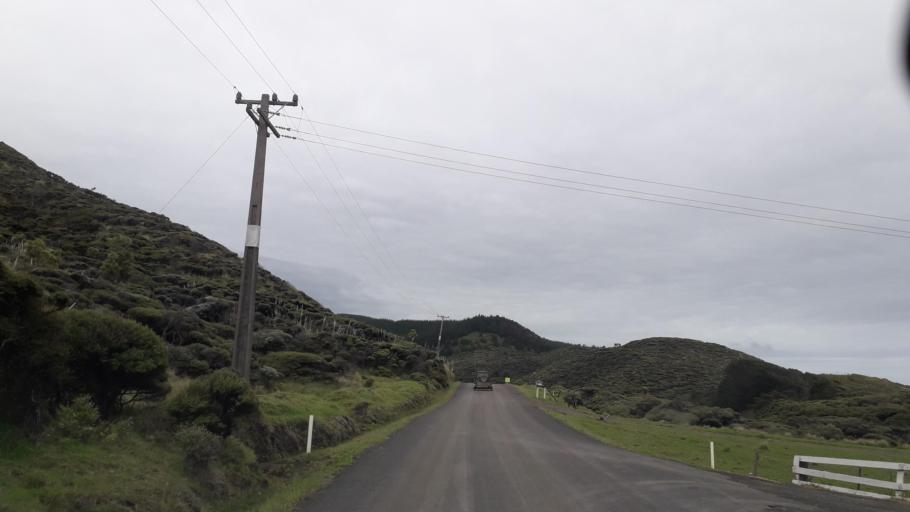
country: NZ
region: Northland
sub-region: Far North District
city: Ahipara
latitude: -35.4366
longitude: 173.2846
